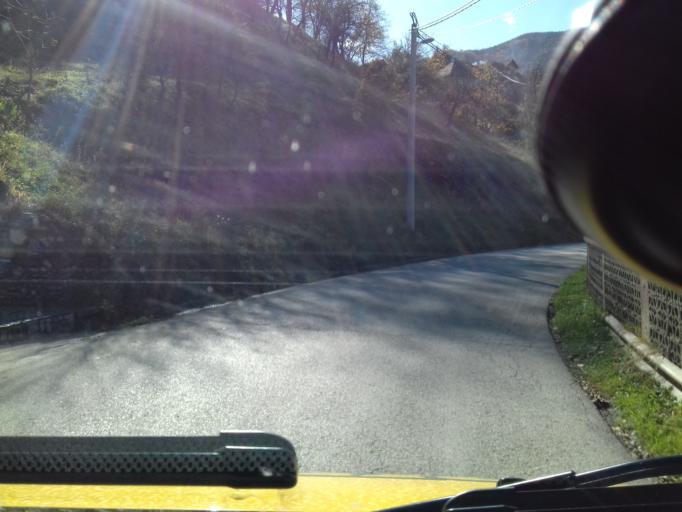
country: BA
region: Federation of Bosnia and Herzegovina
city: Zenica
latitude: 44.1803
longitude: 17.9042
